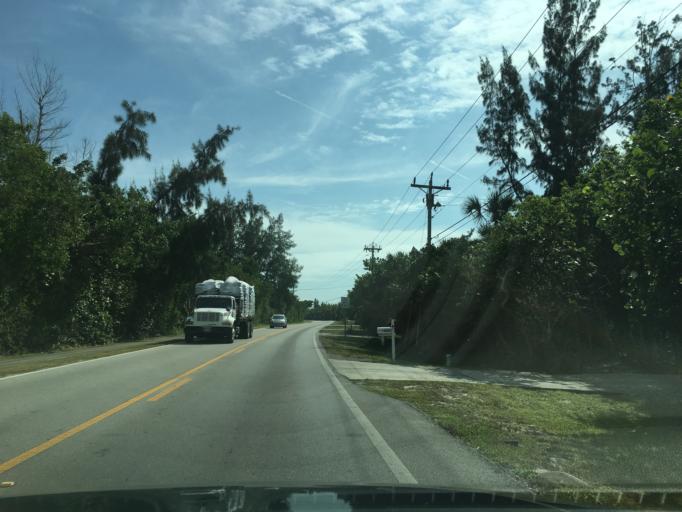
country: US
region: Florida
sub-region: Lee County
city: Saint James City
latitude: 26.4773
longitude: -82.1761
